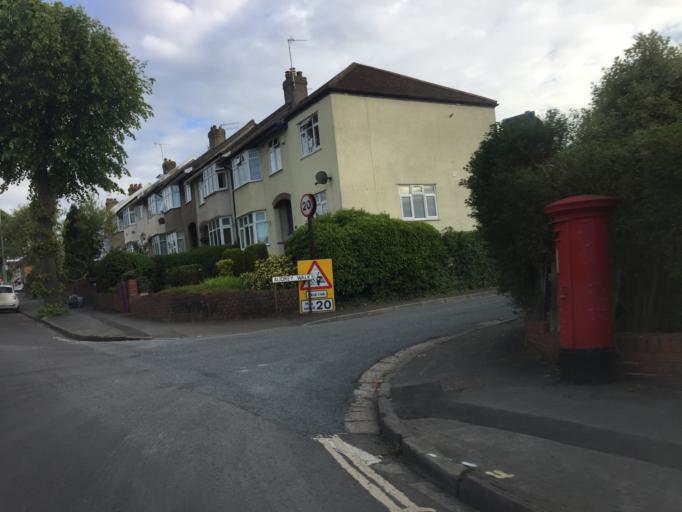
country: GB
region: England
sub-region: Bristol
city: Bristol
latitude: 51.4911
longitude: -2.5956
